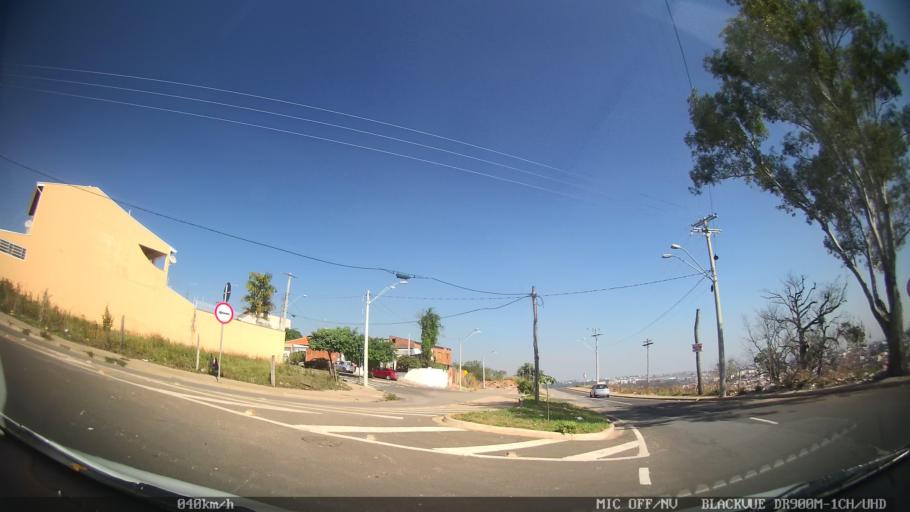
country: BR
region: Sao Paulo
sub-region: Campinas
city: Campinas
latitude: -22.9548
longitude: -47.0814
